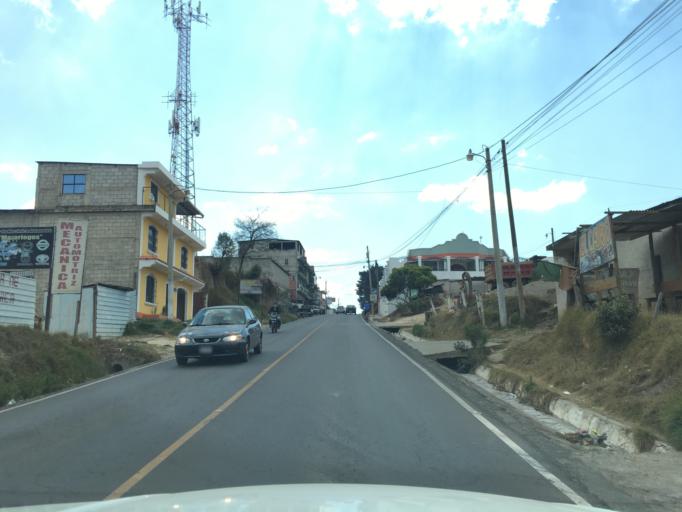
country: GT
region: Quetzaltenango
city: Olintepeque
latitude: 14.8792
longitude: -91.5141
